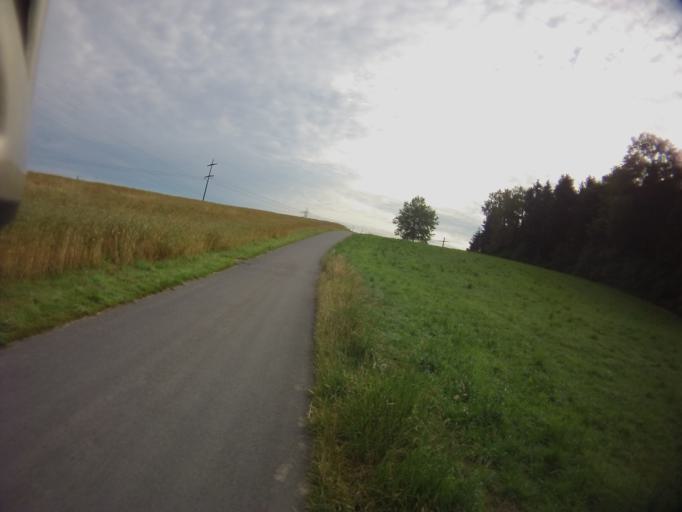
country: CH
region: Zug
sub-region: Zug
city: Cham
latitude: 47.2020
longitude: 8.4666
